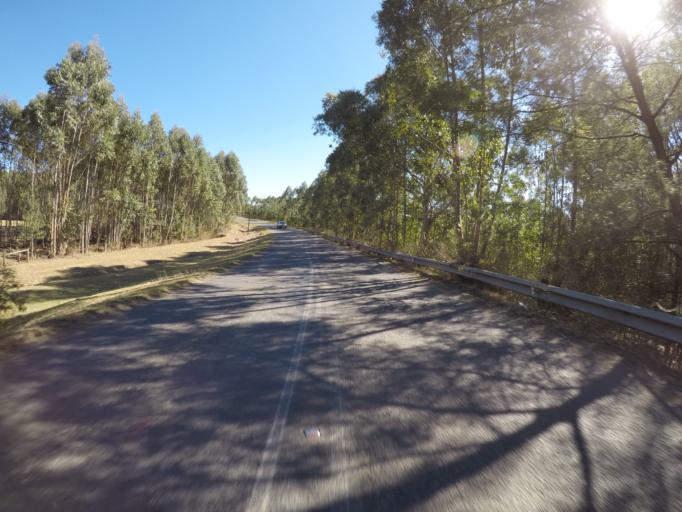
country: ZA
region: Eastern Cape
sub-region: OR Tambo District Municipality
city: Mthatha
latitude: -31.7764
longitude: 28.7377
